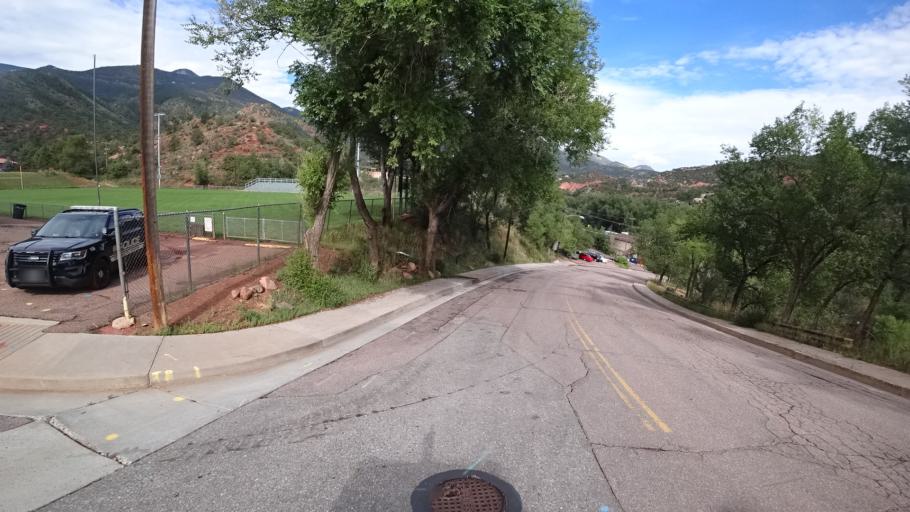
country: US
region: Colorado
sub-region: El Paso County
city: Manitou Springs
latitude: 38.8566
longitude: -104.9047
